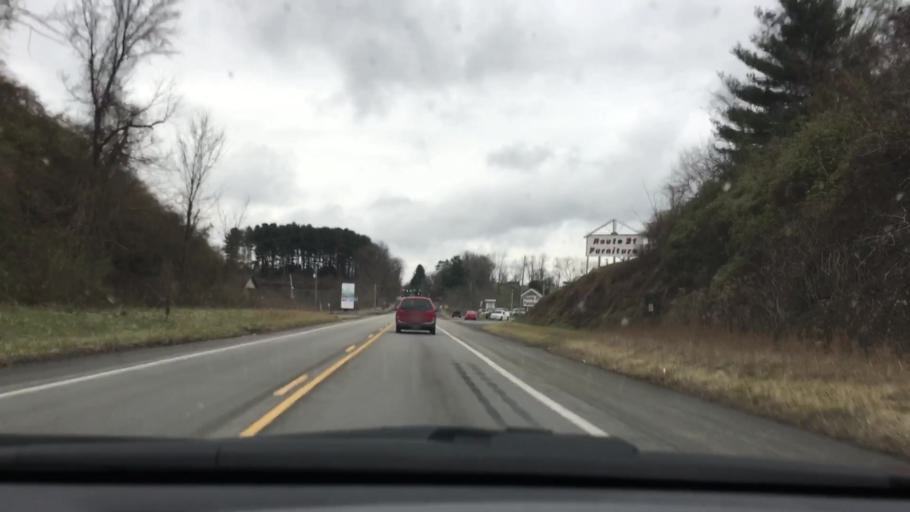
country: US
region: Pennsylvania
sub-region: Fayette County
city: Masontown
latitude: 39.8884
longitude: -79.8590
